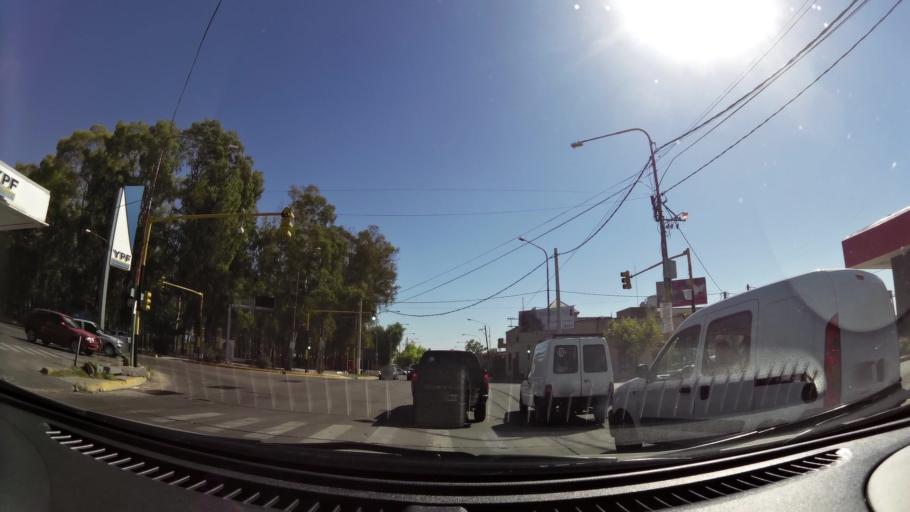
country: AR
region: Mendoza
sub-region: Departamento de Maipu
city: Maipu
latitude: -32.9586
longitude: -68.7896
